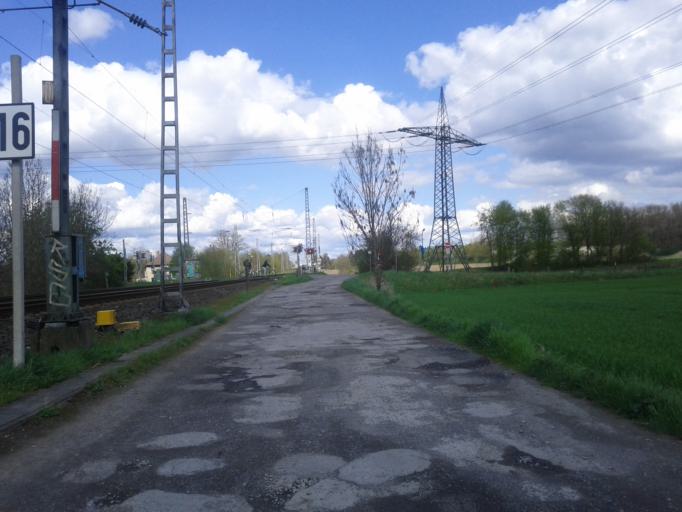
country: DE
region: North Rhine-Westphalia
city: Lanstrop
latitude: 51.5544
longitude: 7.5208
